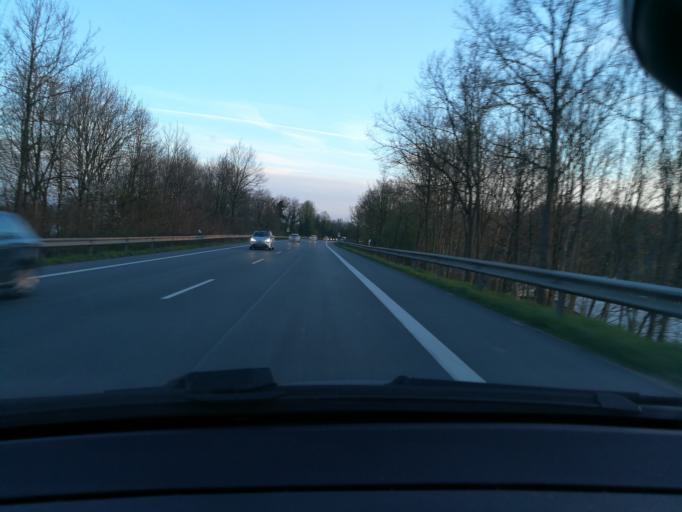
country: DE
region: North Rhine-Westphalia
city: Halle
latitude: 52.0624
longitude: 8.3477
